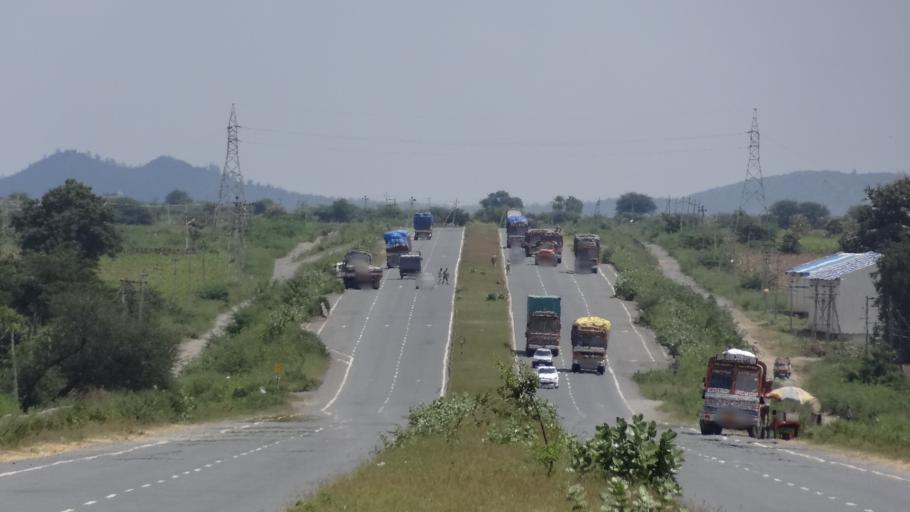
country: IN
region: Karnataka
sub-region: Haveri
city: Haveri
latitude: 14.7771
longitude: 75.3952
